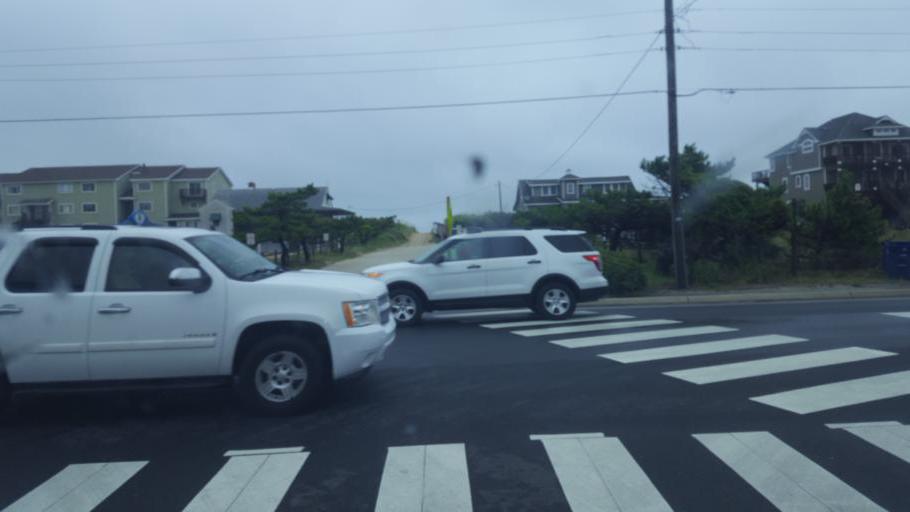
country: US
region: North Carolina
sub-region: Dare County
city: Nags Head
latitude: 35.9942
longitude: -75.6456
